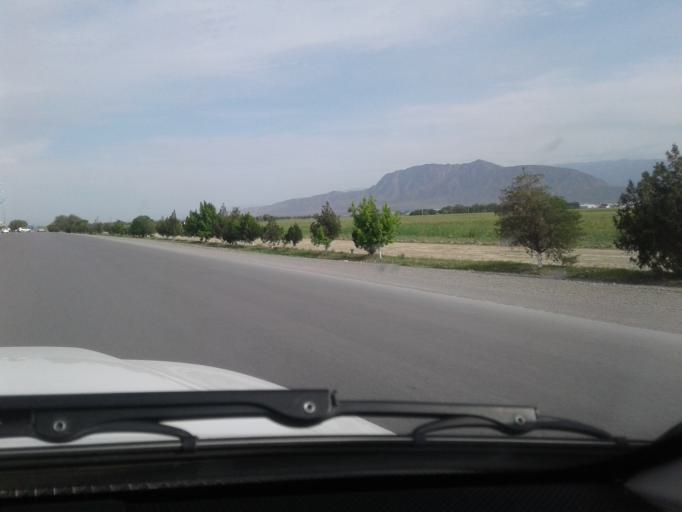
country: TM
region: Ahal
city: Abadan
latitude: 38.1388
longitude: 58.0030
